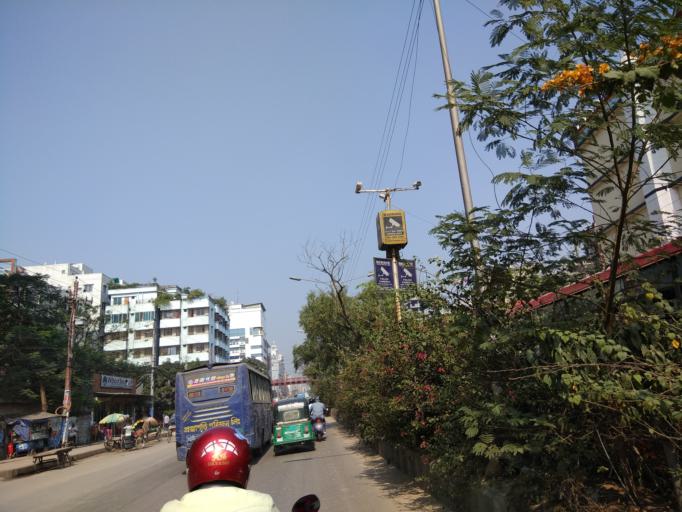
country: BD
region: Dhaka
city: Azimpur
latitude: 23.8132
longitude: 90.3669
